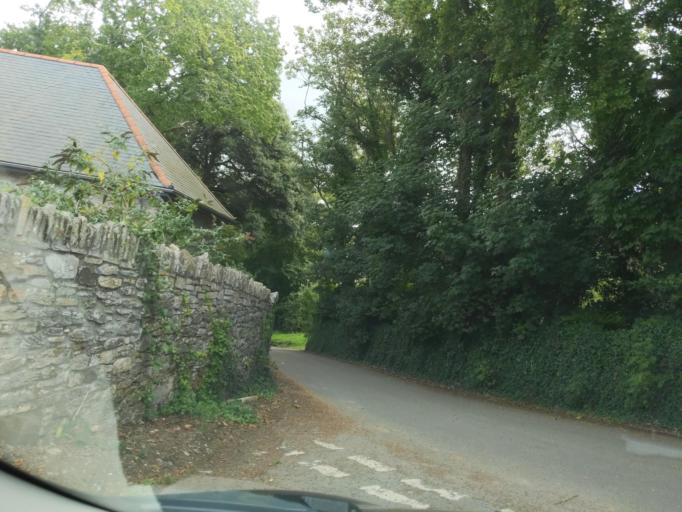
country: GB
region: England
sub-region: Plymouth
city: Plymstock
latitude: 50.3499
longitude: -4.1083
